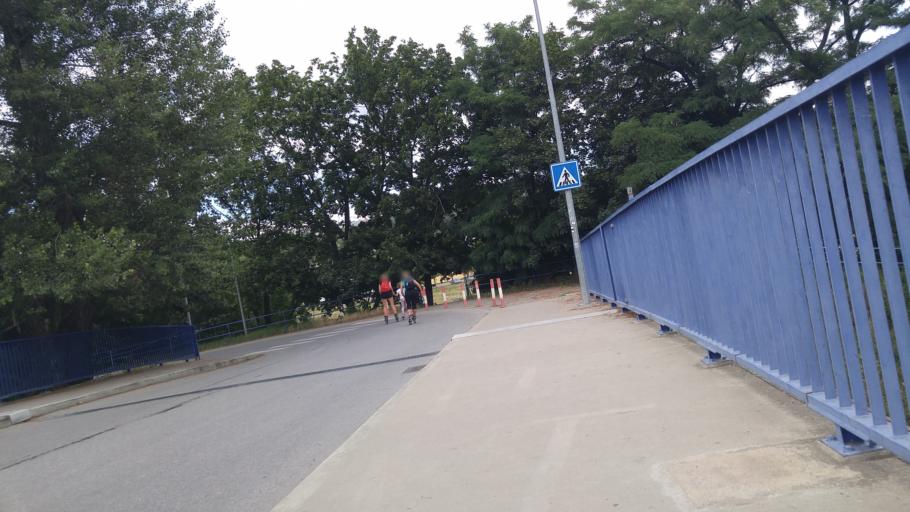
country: CZ
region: Praha
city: Prague
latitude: 50.1110
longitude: 14.4180
